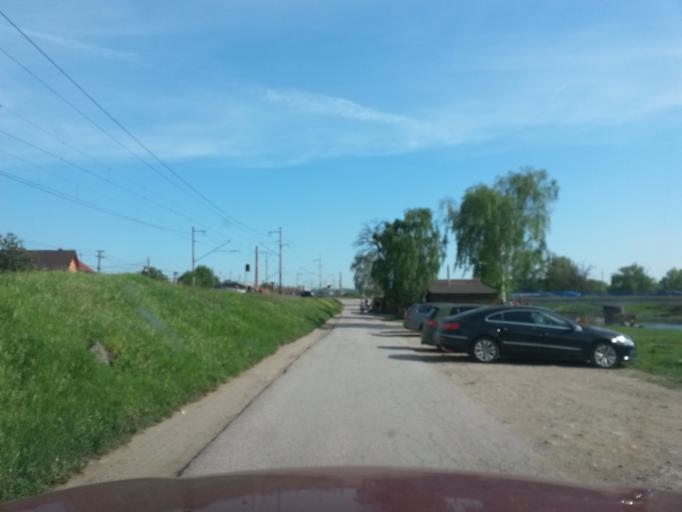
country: SK
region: Kosicky
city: Kosice
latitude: 48.7575
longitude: 21.2516
